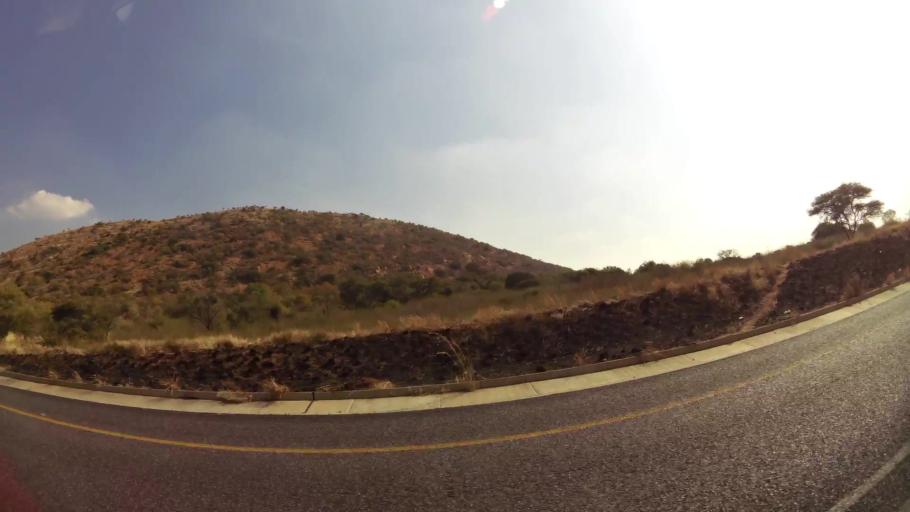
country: ZA
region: North-West
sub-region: Bojanala Platinum District Municipality
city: Rustenburg
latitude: -25.5716
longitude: 27.1399
